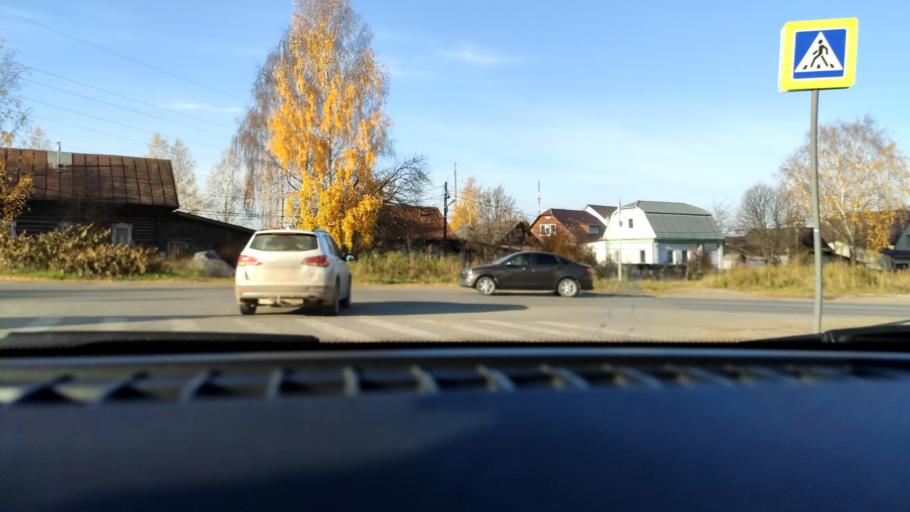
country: RU
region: Perm
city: Perm
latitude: 58.0118
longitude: 56.3203
